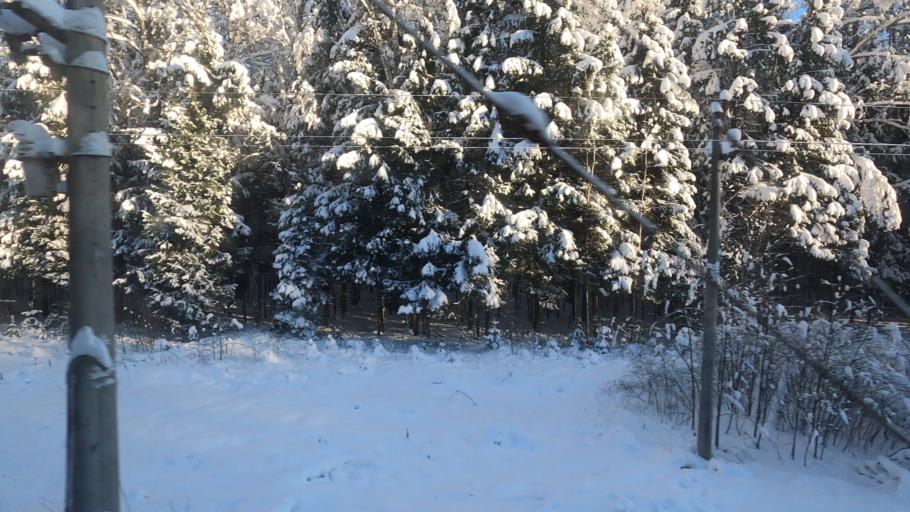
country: RU
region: Moskovskaya
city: Novo-Nikol'skoye
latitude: 56.6335
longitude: 37.5628
